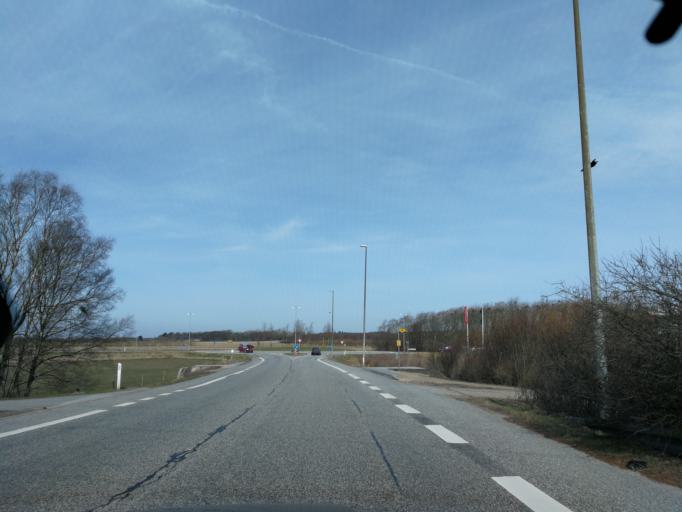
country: DK
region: North Denmark
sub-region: Alborg Kommune
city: Vodskov
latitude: 57.0994
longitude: 10.0190
